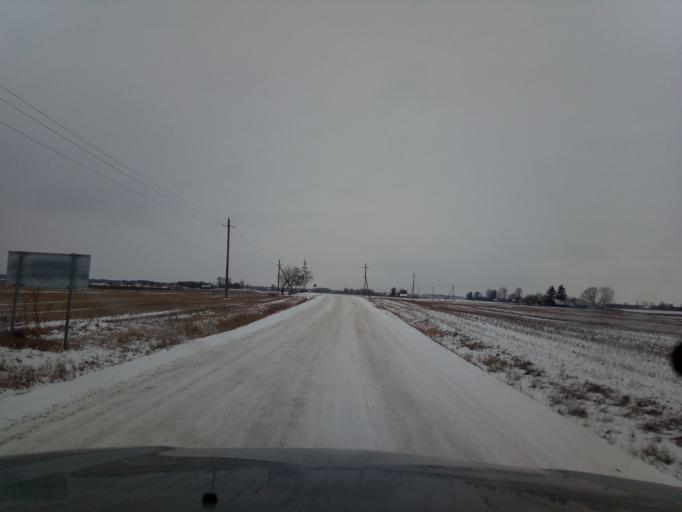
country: LT
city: Ramygala
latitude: 55.4963
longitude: 24.5294
